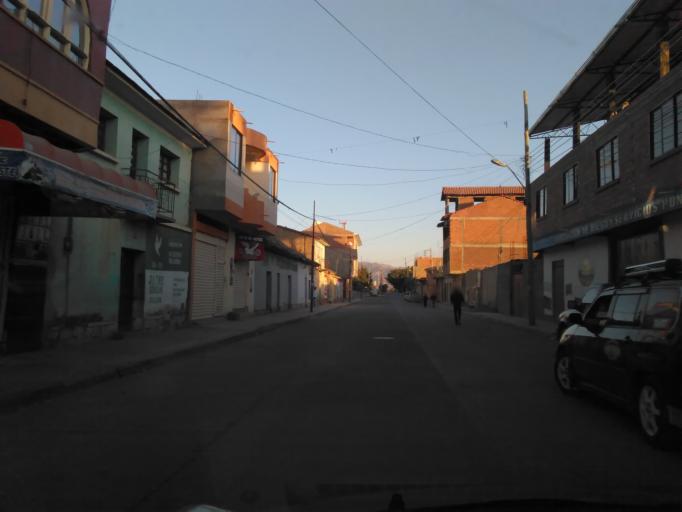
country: BO
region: Cochabamba
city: Punata
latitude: -17.5492
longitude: -65.8358
